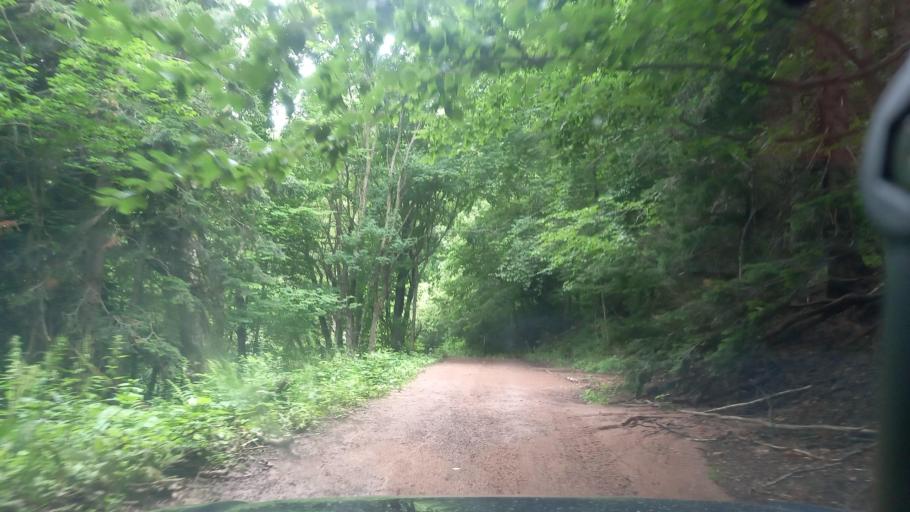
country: RU
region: Karachayevo-Cherkesiya
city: Kurdzhinovo
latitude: 43.8084
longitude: 40.8550
